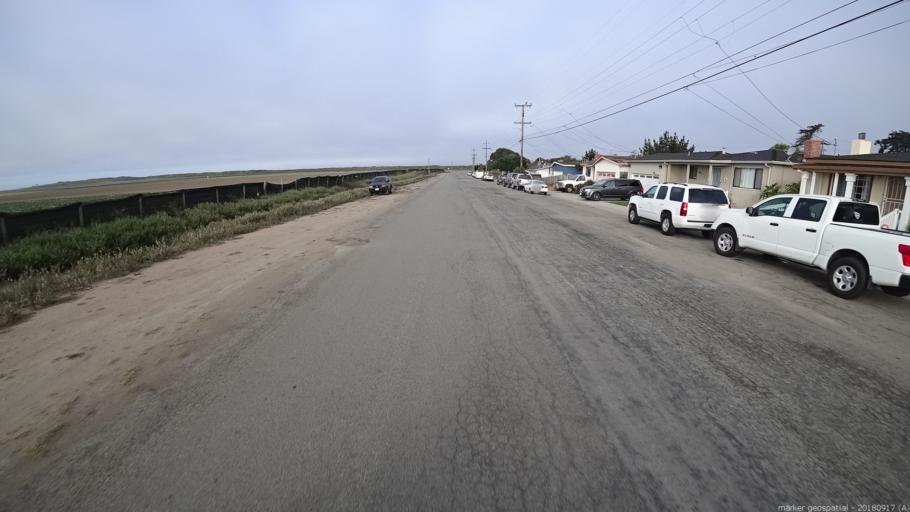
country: US
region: California
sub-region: Monterey County
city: Castroville
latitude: 36.7906
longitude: -121.7854
